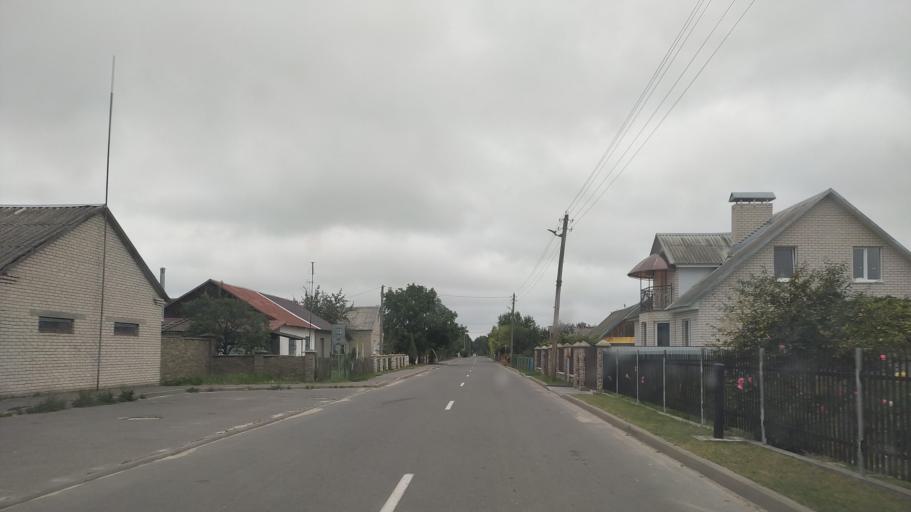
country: BY
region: Brest
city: Byaroza
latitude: 52.5309
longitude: 24.9690
